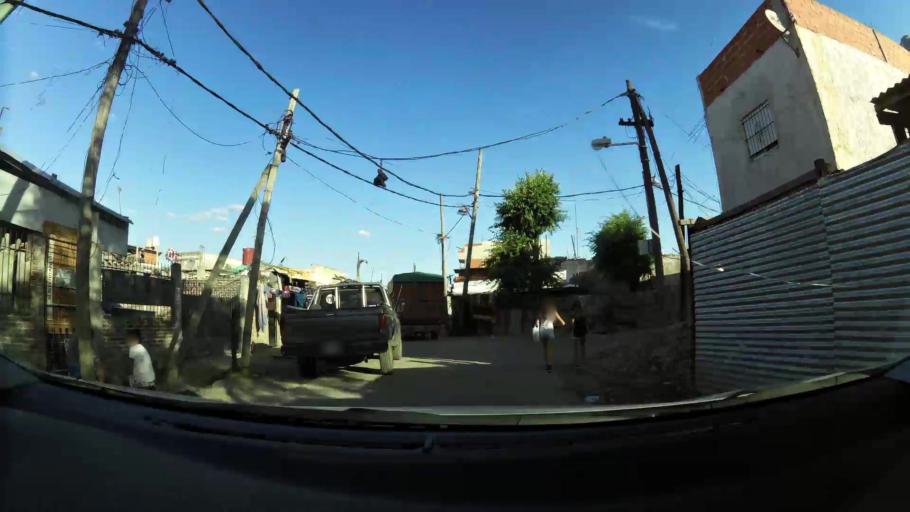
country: AR
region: Buenos Aires F.D.
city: Villa Lugano
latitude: -34.7074
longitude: -58.4862
